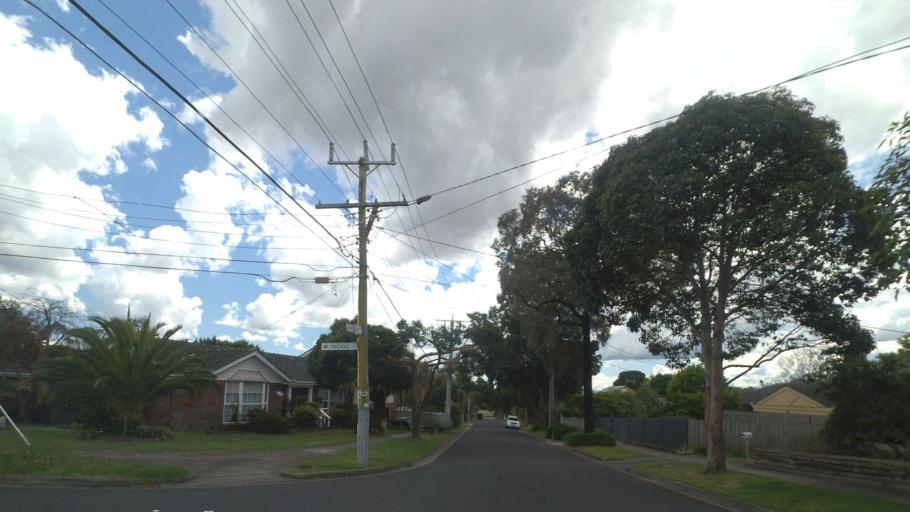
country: AU
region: Victoria
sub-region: Maroondah
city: Croydon South
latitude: -37.8141
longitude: 145.2758
